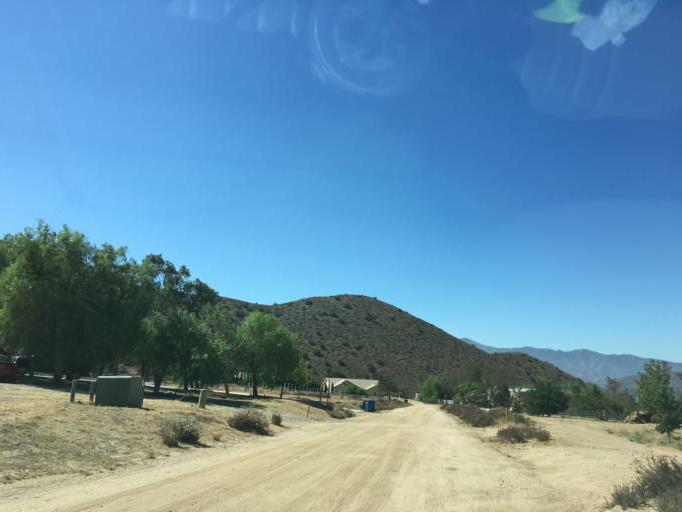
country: US
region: California
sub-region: Los Angeles County
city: Acton
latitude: 34.5060
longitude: -118.1919
